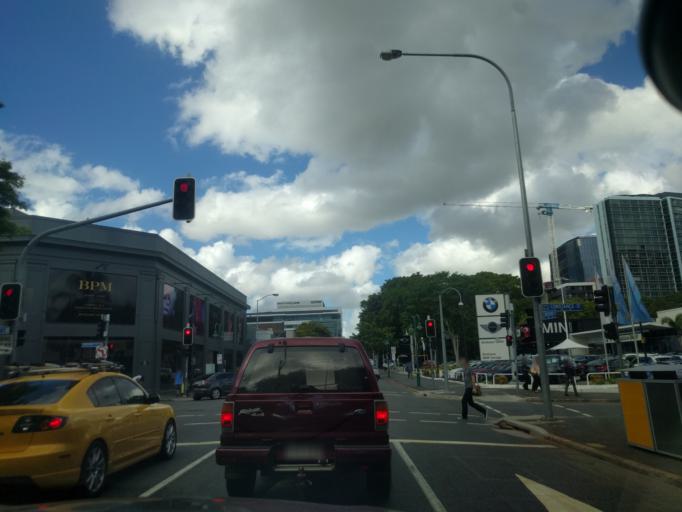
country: AU
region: Queensland
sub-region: Brisbane
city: Fortitude Valley
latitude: -27.4556
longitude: 153.0356
